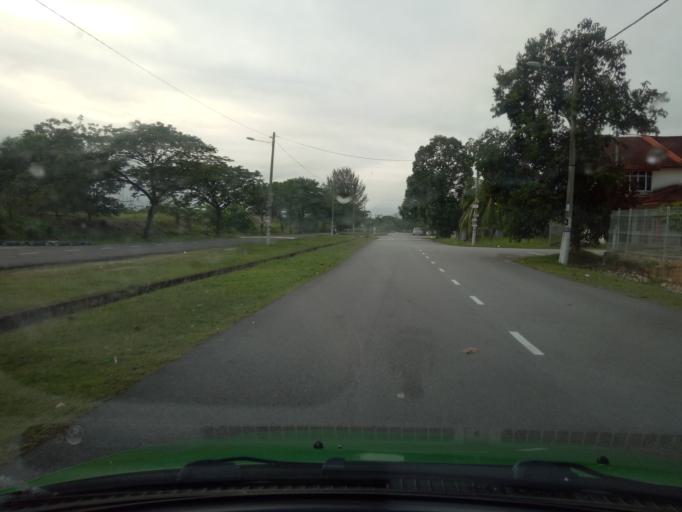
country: MY
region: Selangor
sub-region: Hulu Langat
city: Semenyih
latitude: 2.9313
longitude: 101.8636
